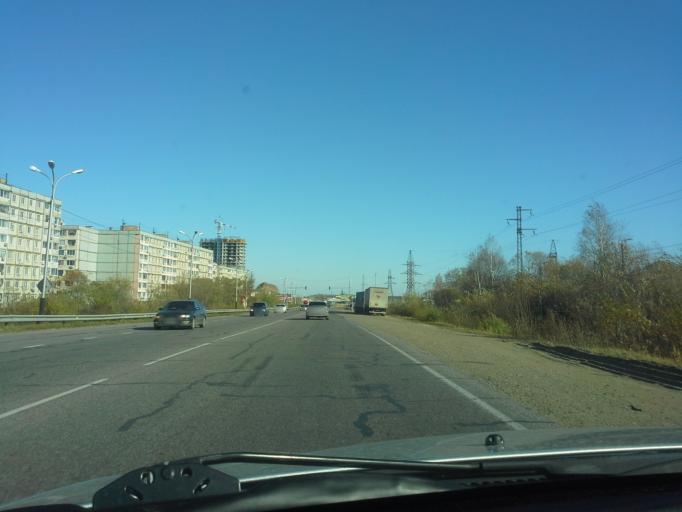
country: RU
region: Khabarovsk Krai
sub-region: Khabarovskiy Rayon
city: Khabarovsk
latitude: 48.5472
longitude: 135.0466
